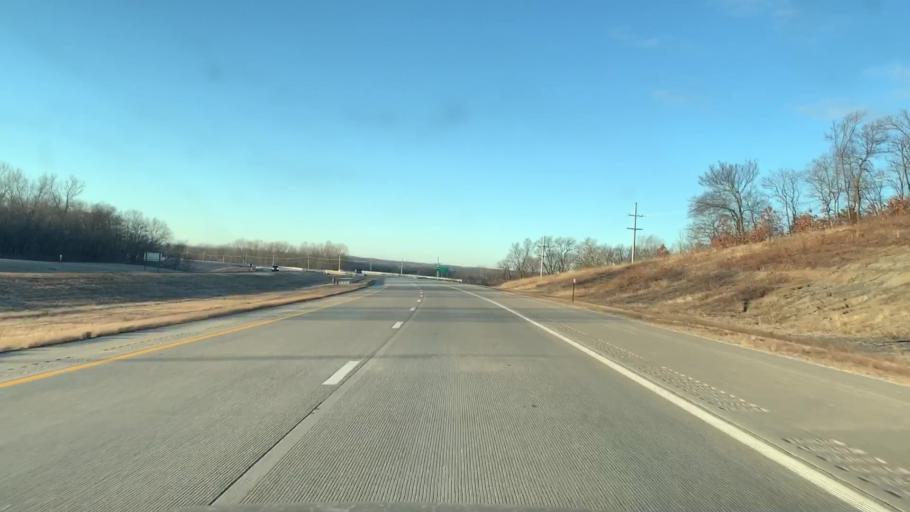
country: US
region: Kansas
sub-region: Linn County
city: Pleasanton
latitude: 38.2509
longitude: -94.6849
